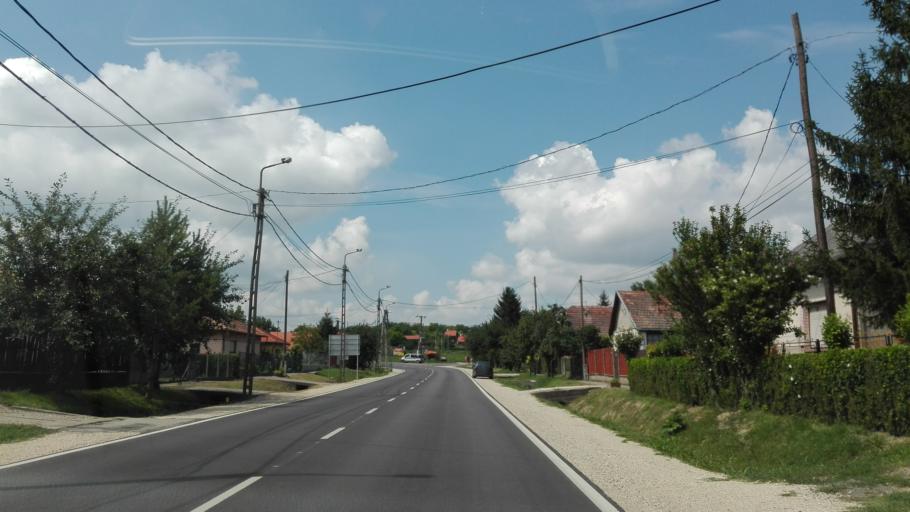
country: HU
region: Tolna
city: Simontornya
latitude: 46.7593
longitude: 18.5414
